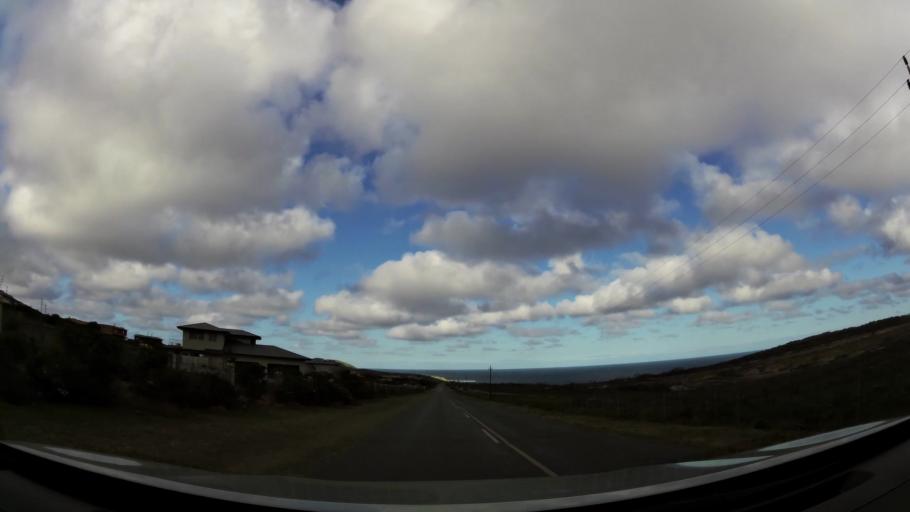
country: ZA
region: Western Cape
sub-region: Eden District Municipality
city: Plettenberg Bay
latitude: -34.0923
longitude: 23.3594
